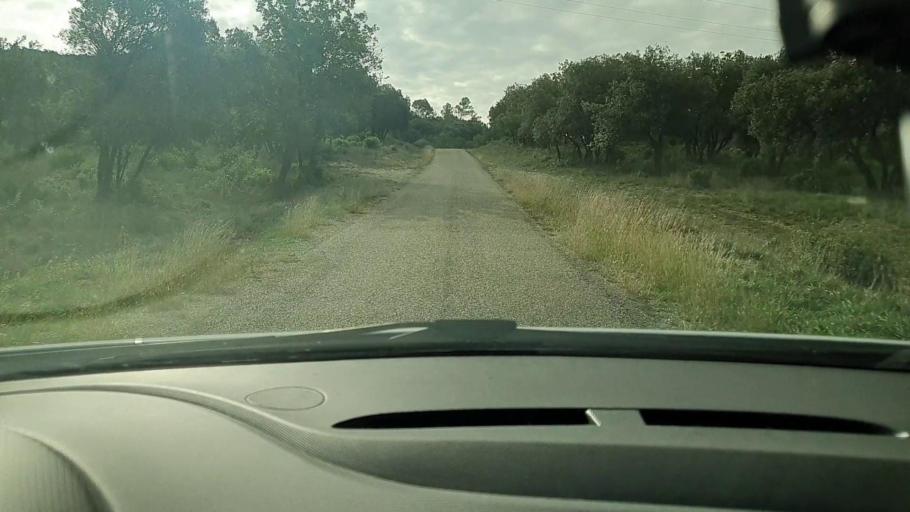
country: FR
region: Languedoc-Roussillon
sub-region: Departement du Gard
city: Montaren-et-Saint-Mediers
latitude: 44.0985
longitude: 4.3182
